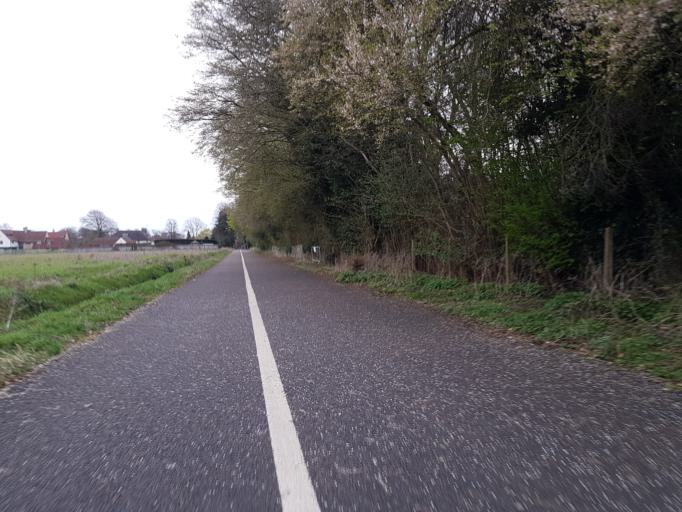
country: GB
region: England
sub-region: Cambridgeshire
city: Girton
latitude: 52.2173
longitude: 0.0956
